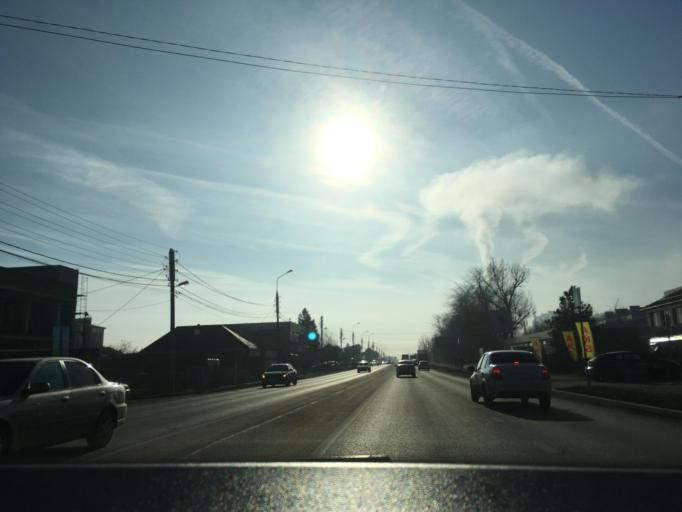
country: RU
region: Krasnodarskiy
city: Krasnodar
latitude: 45.0983
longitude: 39.0133
